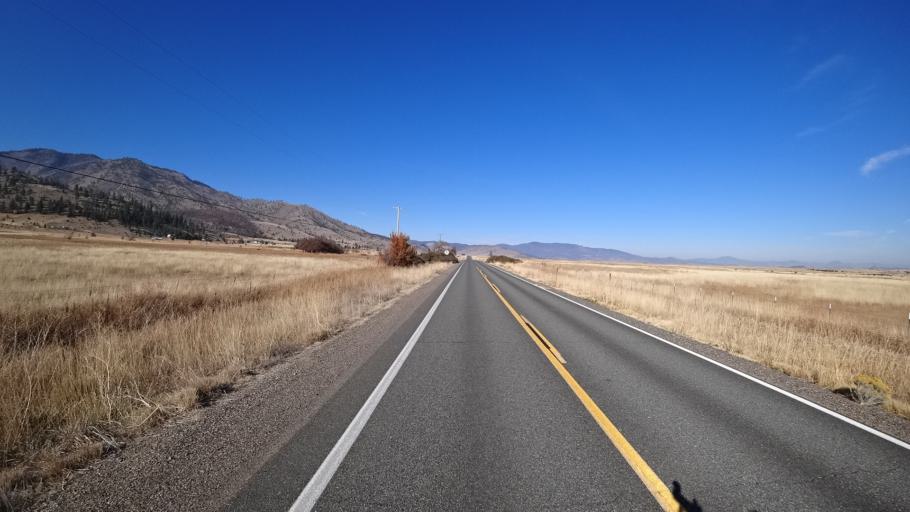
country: US
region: California
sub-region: Siskiyou County
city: Weed
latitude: 41.4699
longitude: -122.4761
